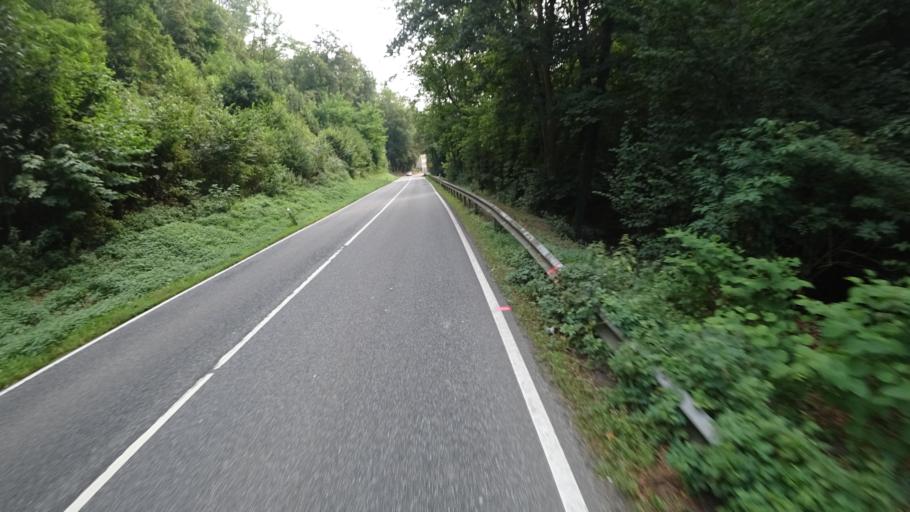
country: DE
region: Rheinland-Pfalz
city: Vallendar
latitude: 50.4068
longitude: 7.6274
